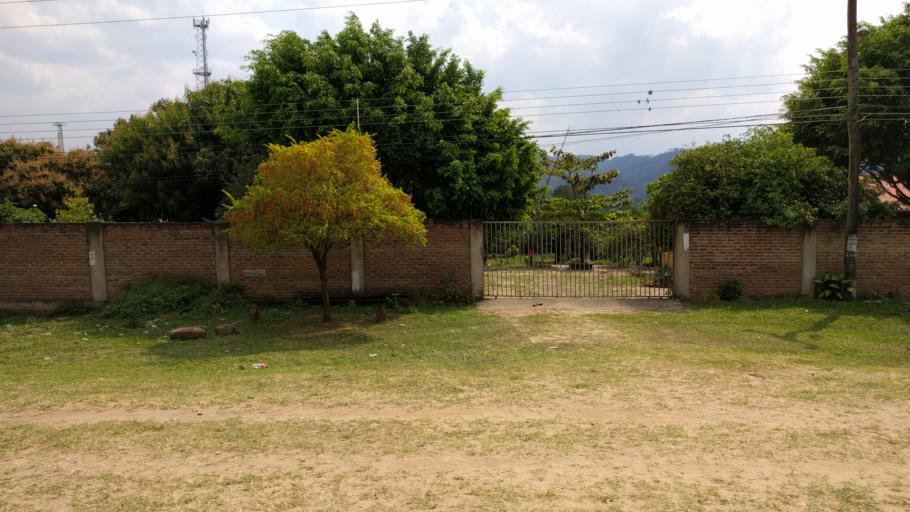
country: BO
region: Santa Cruz
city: Limoncito
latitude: -18.0240
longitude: -63.4004
